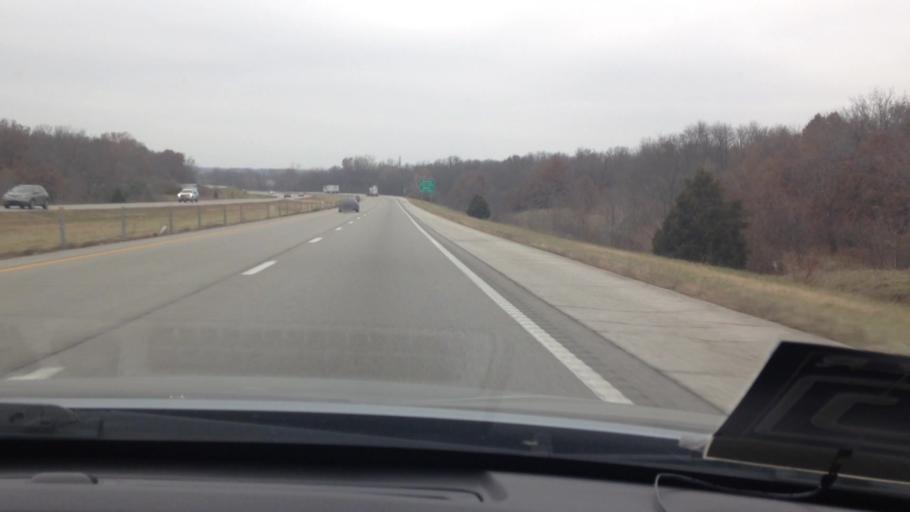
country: US
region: Missouri
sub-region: Cass County
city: Peculiar
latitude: 38.7538
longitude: -94.4807
